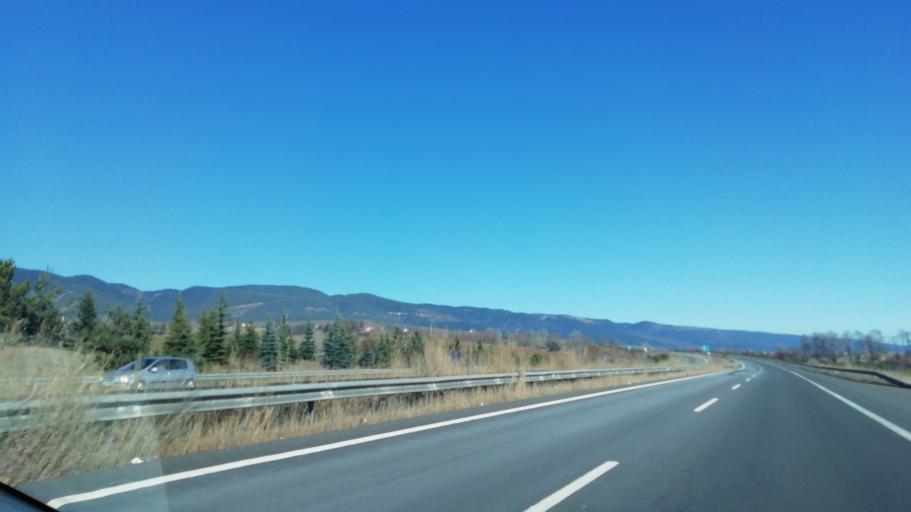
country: TR
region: Bolu
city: Gerede
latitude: 40.7874
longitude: 32.2256
